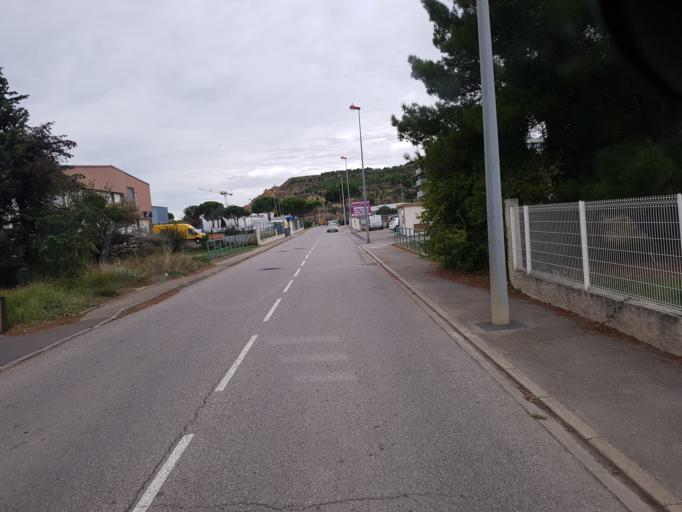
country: FR
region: Languedoc-Roussillon
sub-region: Departement de l'Aude
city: Narbonne
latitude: 43.1594
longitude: 2.9787
